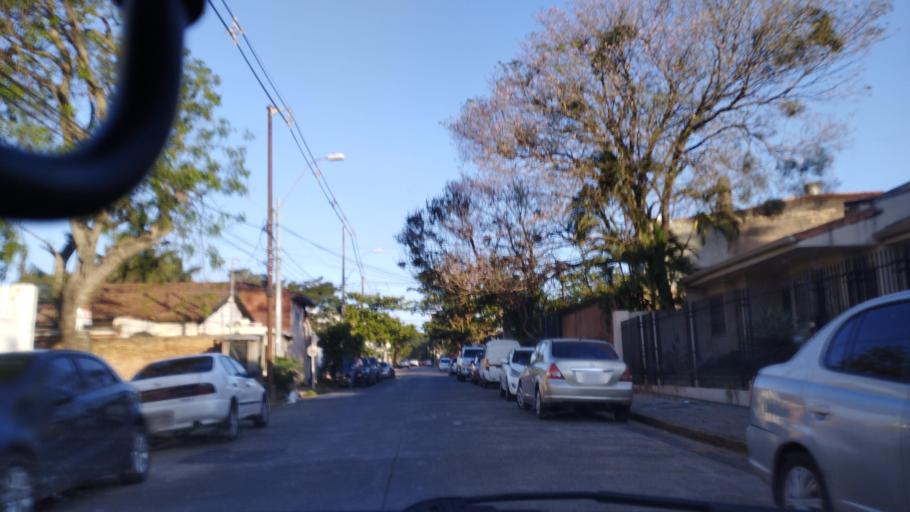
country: PY
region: Central
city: Lambare
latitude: -25.3022
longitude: -57.5846
